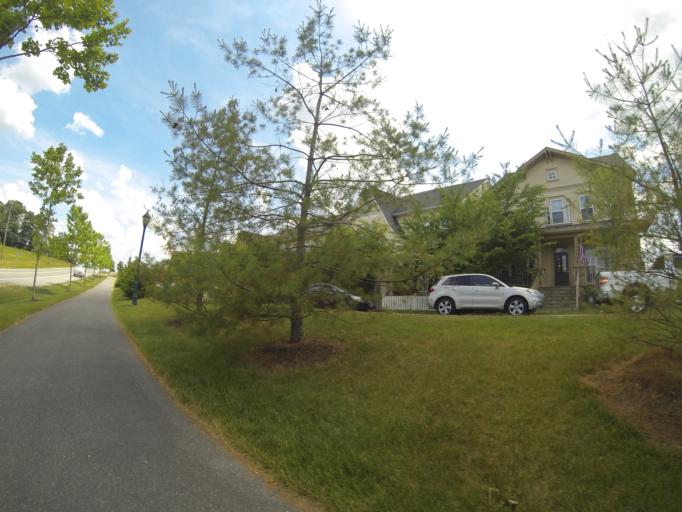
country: US
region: Maryland
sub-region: Montgomery County
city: Clarksburg
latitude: 39.2478
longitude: -77.2695
